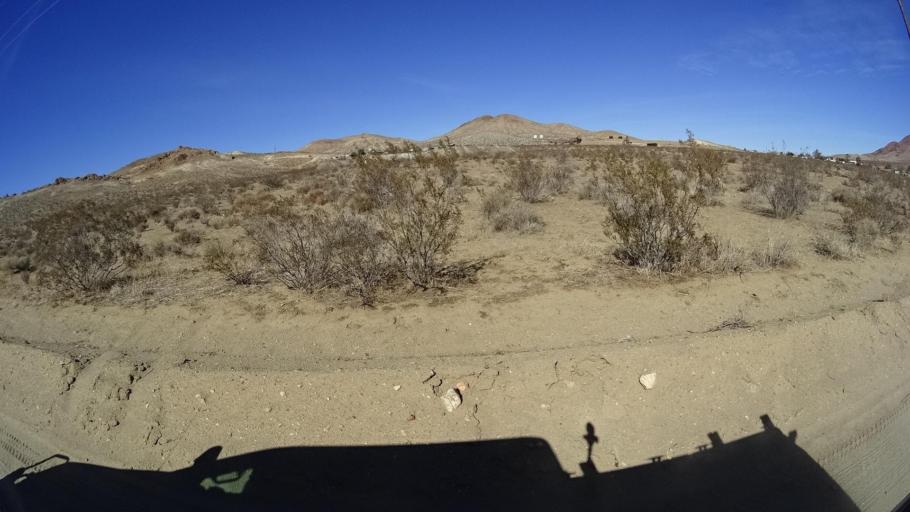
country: US
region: California
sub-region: Kern County
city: Ridgecrest
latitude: 35.3466
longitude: -117.6230
